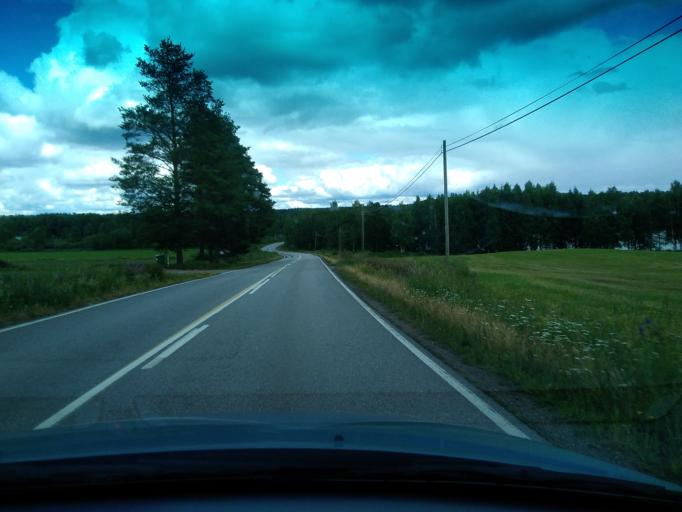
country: FI
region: Central Finland
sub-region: Saarijaervi-Viitasaari
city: Saarijaervi
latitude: 62.7349
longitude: 25.1613
